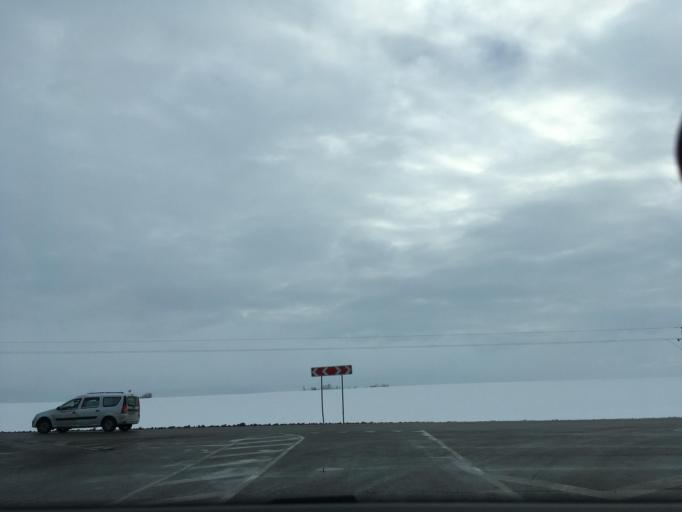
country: UA
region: Luhansk
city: Lozno-Oleksandrivka
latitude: 49.9516
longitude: 38.9557
